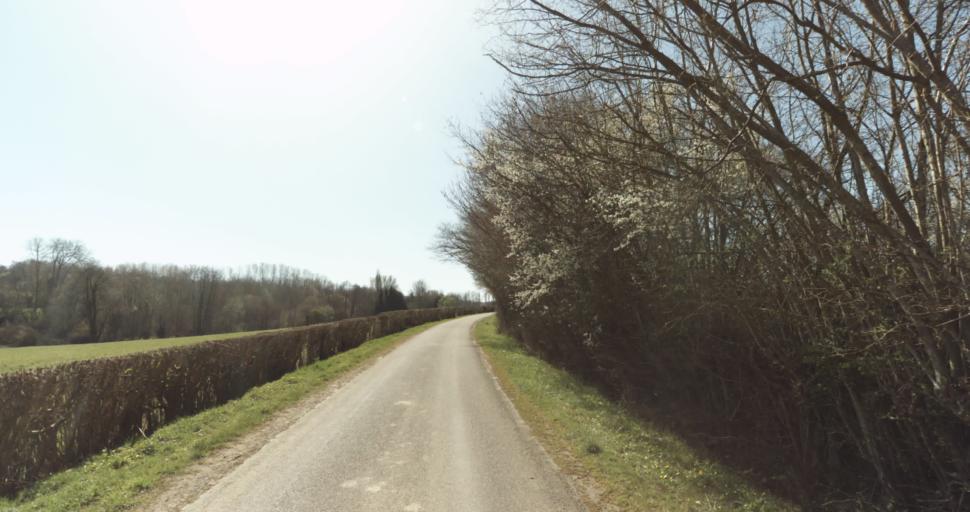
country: FR
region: Lower Normandy
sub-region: Departement du Calvados
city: Livarot
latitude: 49.0102
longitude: 0.0743
